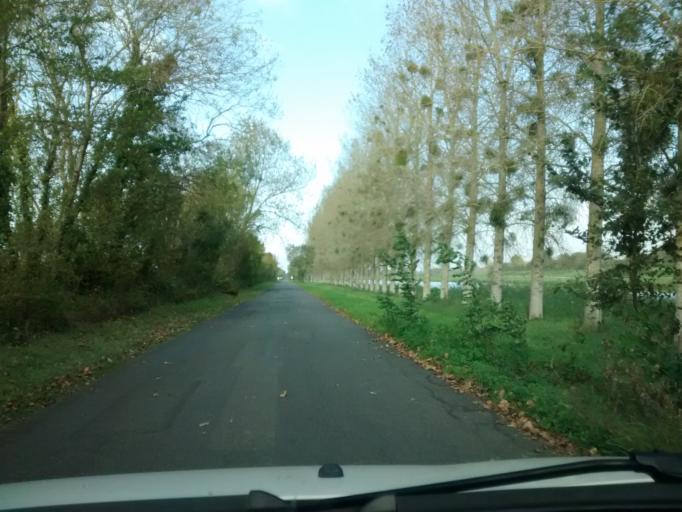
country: FR
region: Pays de la Loire
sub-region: Departement de la Loire-Atlantique
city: Vue
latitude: 47.2389
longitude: -1.8737
